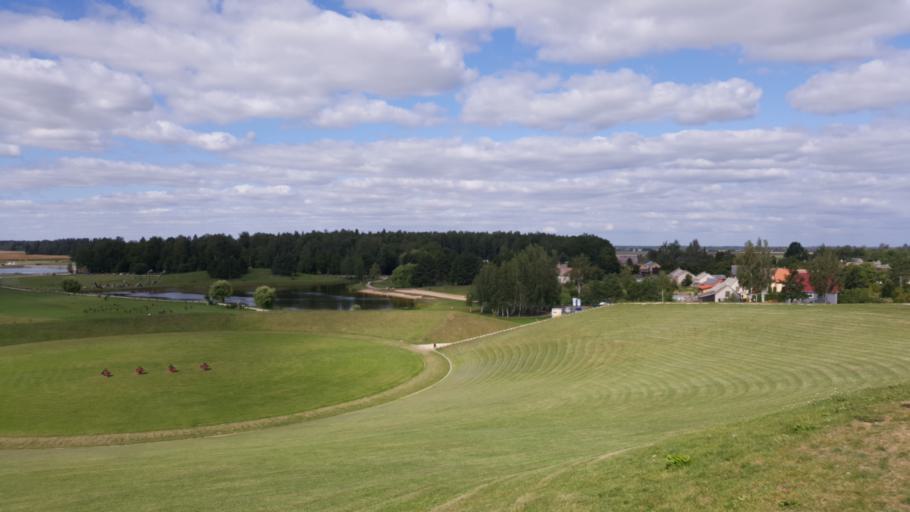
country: LT
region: Siauliu apskritis
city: Radviliskis
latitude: 56.0205
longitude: 23.5092
